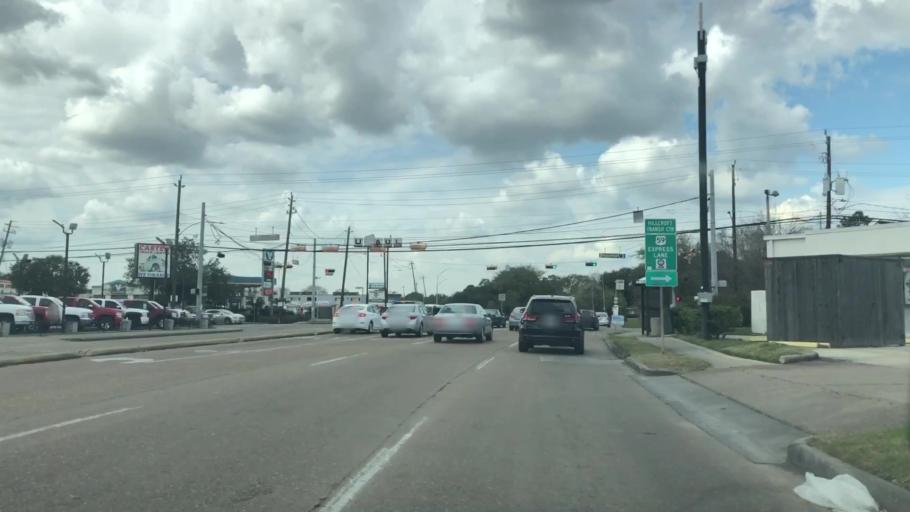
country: US
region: Texas
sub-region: Harris County
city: Bellaire
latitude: 29.6894
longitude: -95.5023
